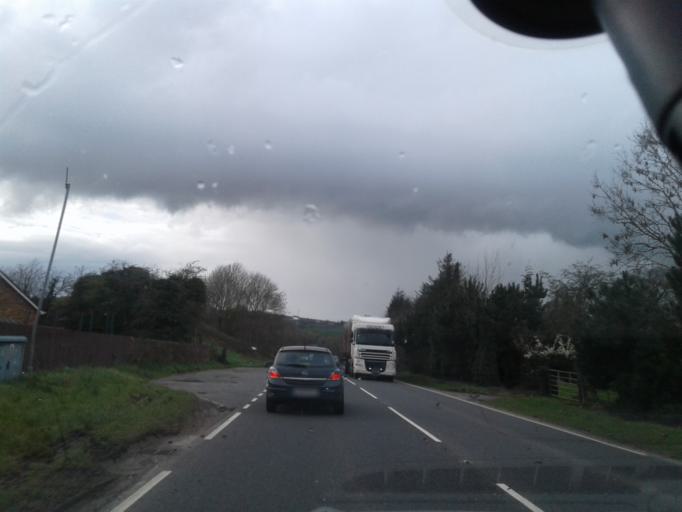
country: GB
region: Northern Ireland
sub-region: Strabane District
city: Sion Mills
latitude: 54.7608
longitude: -7.4577
